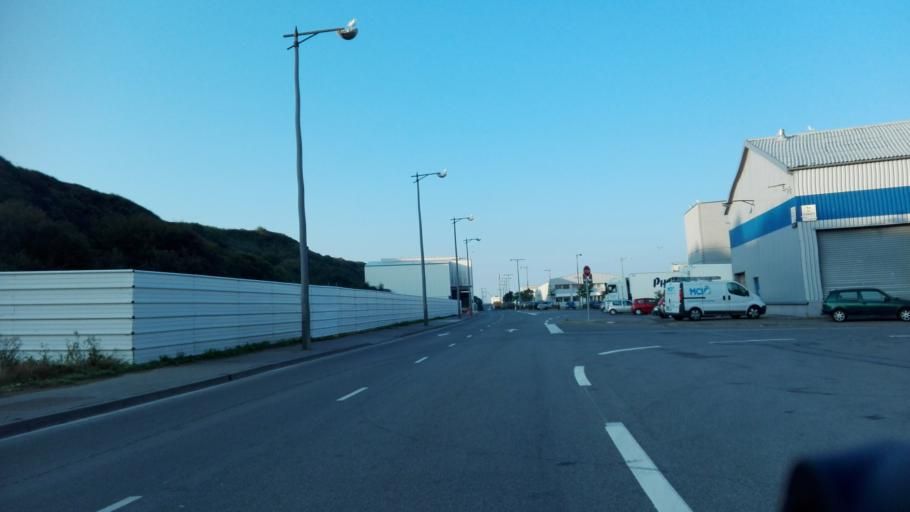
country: FR
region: Nord-Pas-de-Calais
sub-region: Departement du Pas-de-Calais
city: Outreau
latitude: 50.7209
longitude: 1.5833
